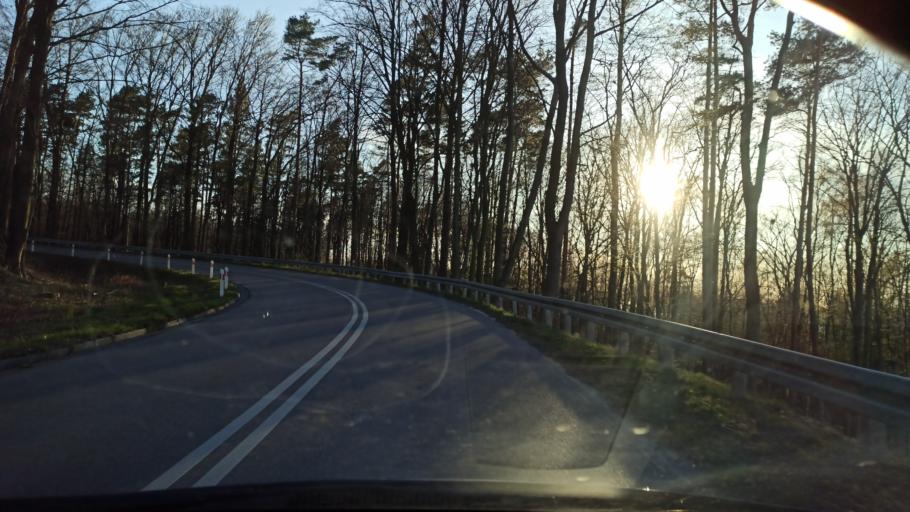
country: PL
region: Warmian-Masurian Voivodeship
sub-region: Powiat elblaski
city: Tolkmicko
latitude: 54.2916
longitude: 19.4697
